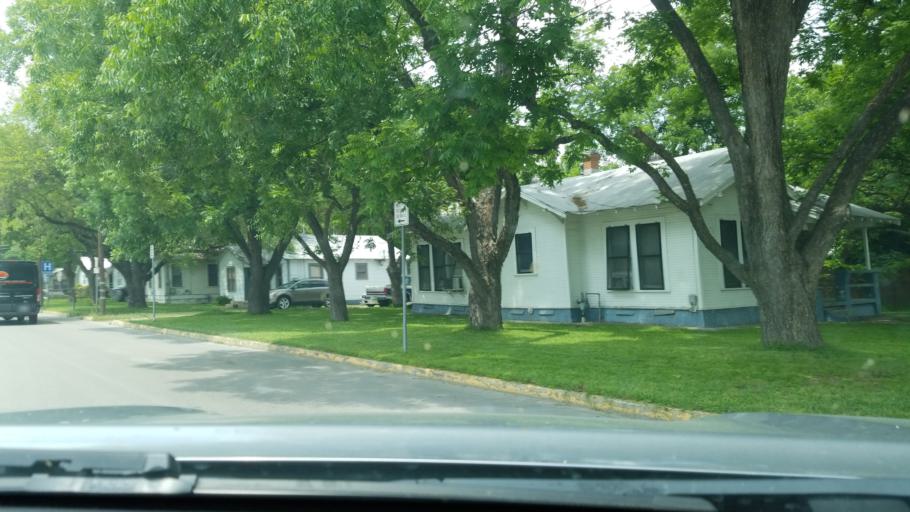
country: US
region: Texas
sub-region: Comal County
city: New Braunfels
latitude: 29.7046
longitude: -98.1162
